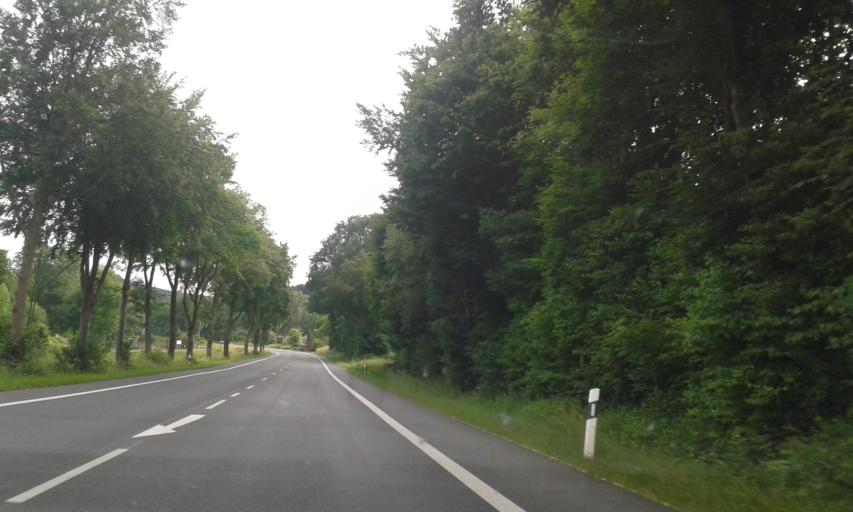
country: DE
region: North Rhine-Westphalia
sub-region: Regierungsbezirk Detmold
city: Barntrup
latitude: 52.0659
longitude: 9.1013
